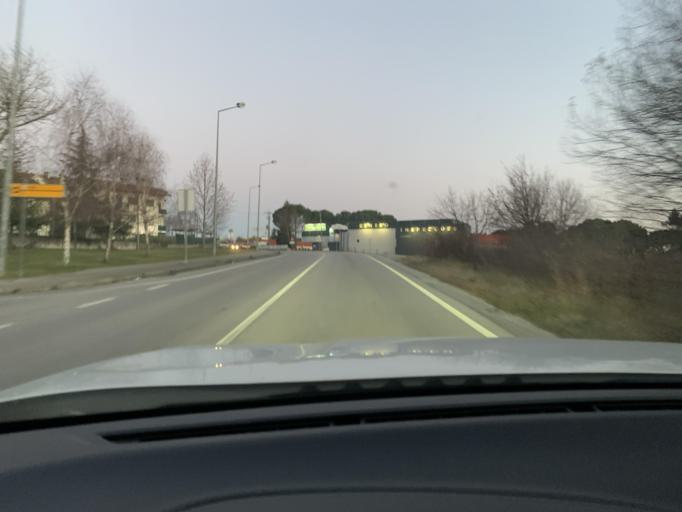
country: PT
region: Viseu
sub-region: Viseu
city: Viseu
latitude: 40.6316
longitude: -7.9040
